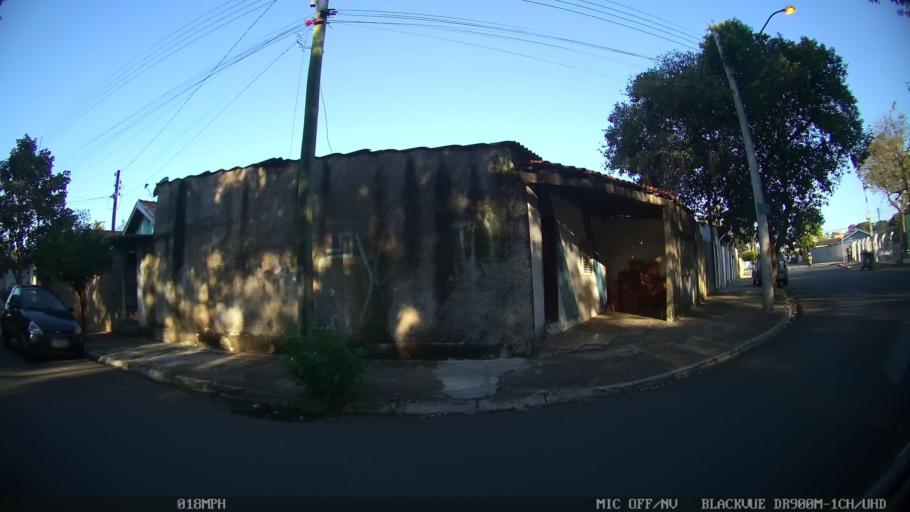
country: BR
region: Sao Paulo
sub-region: Nova Odessa
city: Nova Odessa
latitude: -22.7852
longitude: -47.2857
